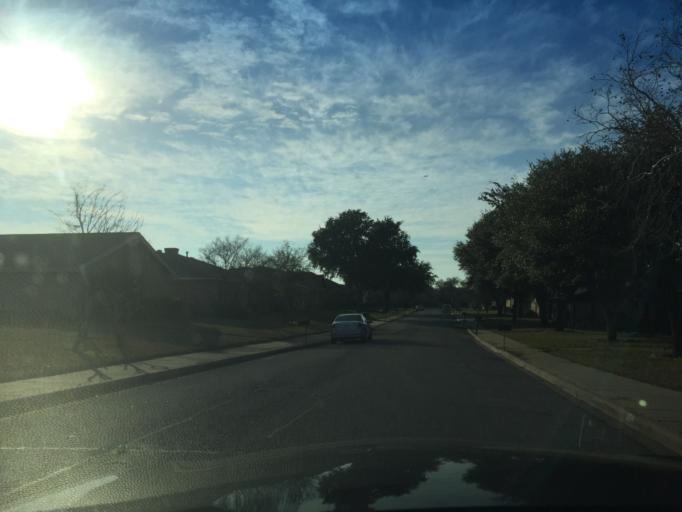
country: US
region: Texas
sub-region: Dallas County
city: Carrollton
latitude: 32.9923
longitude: -96.8771
